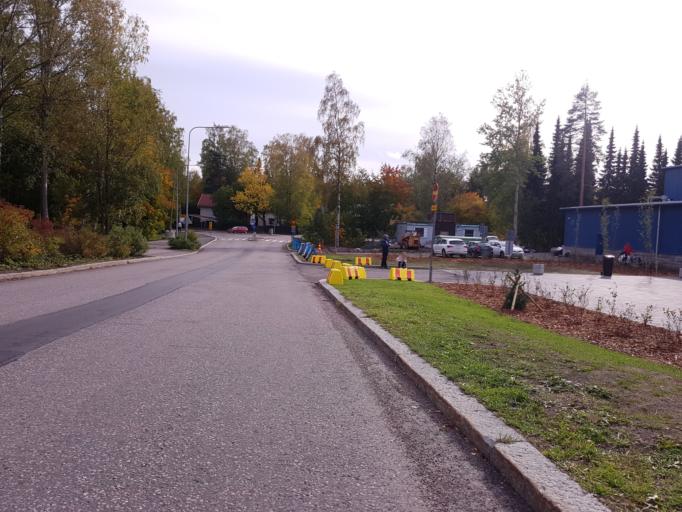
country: FI
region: Uusimaa
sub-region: Helsinki
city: Teekkarikylae
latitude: 60.2461
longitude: 24.8923
